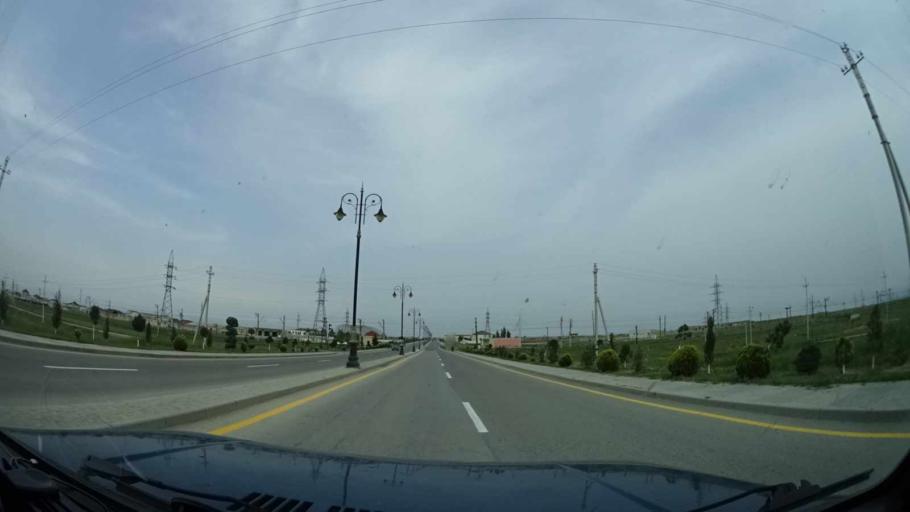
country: AZ
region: Siazan Rayon
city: Kyzyl-Burun
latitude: 41.0666
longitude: 49.1234
